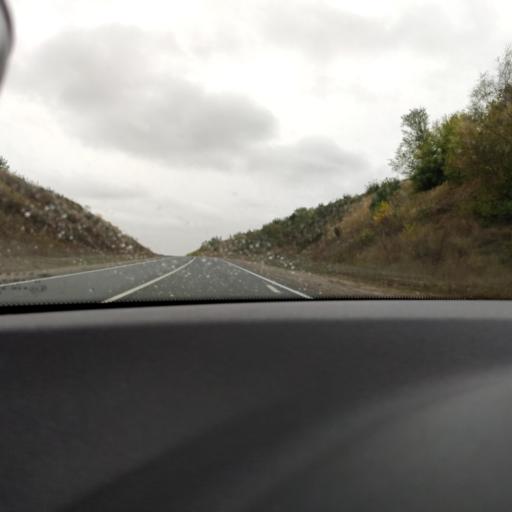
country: RU
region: Samara
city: Mirnyy
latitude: 53.6009
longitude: 50.2759
